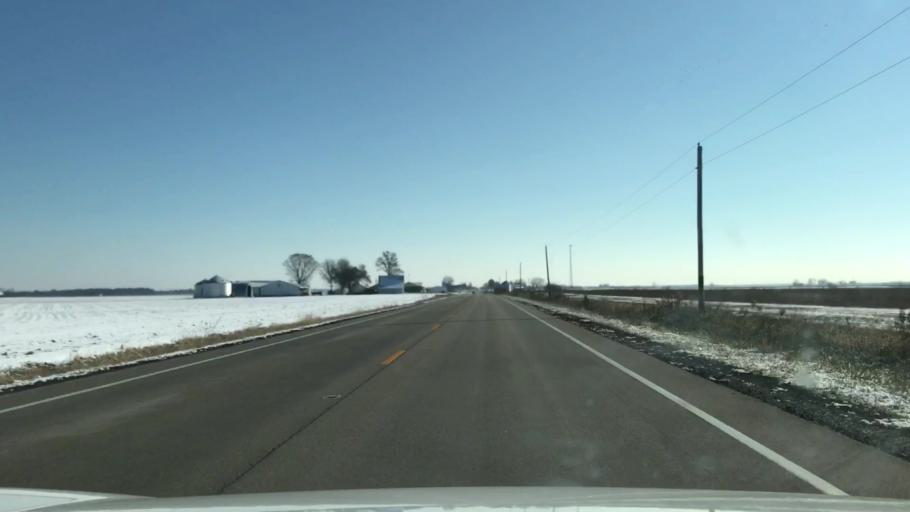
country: US
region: Illinois
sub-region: Washington County
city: Okawville
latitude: 38.4425
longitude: -89.5135
